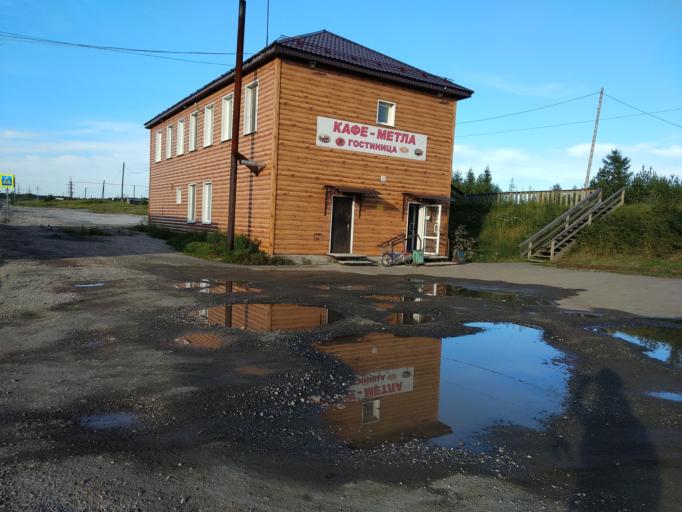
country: RU
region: Sverdlovsk
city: Cheremukhovo
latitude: 60.3359
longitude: 59.9866
